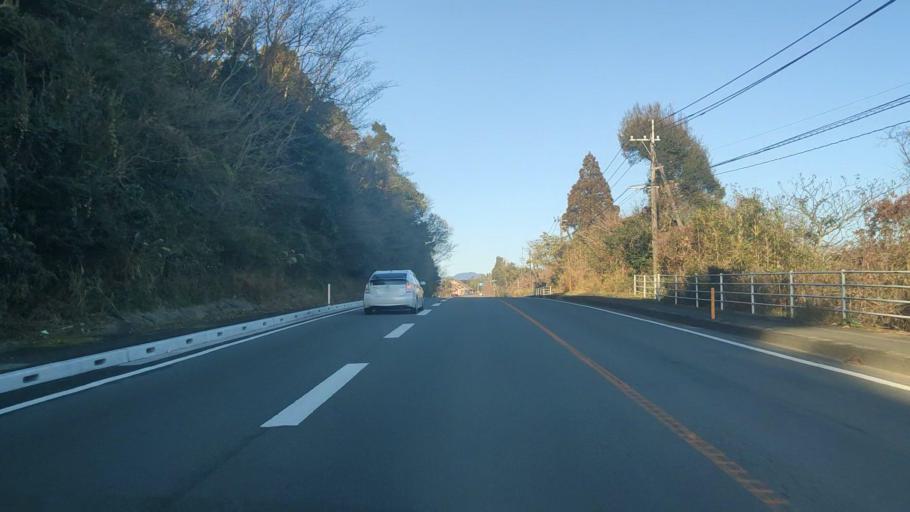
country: JP
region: Miyazaki
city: Takanabe
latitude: 32.1525
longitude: 131.5219
